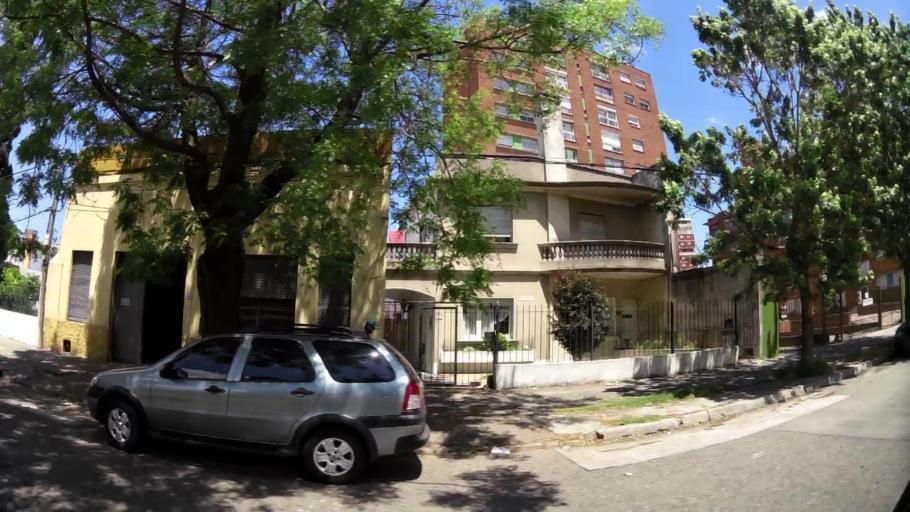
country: UY
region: Montevideo
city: Montevideo
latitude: -34.8710
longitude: -56.2050
